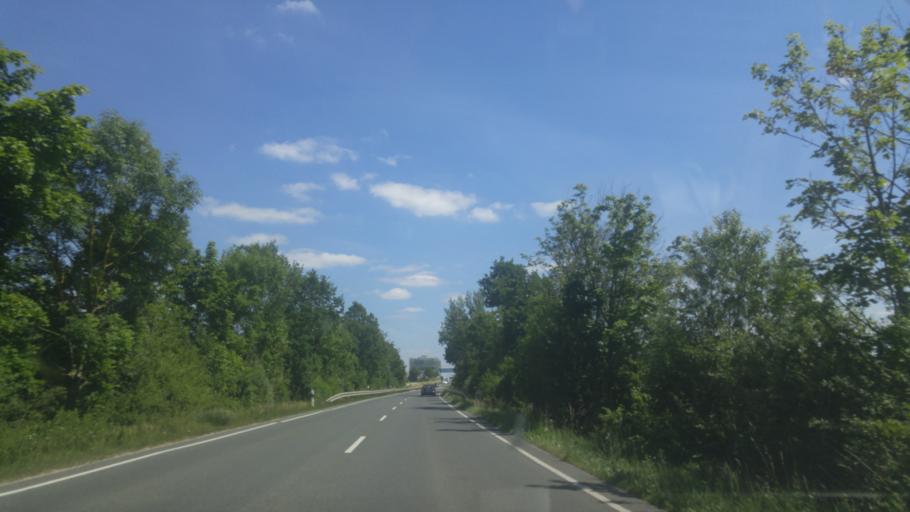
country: DE
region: Bavaria
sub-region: Regierungsbezirk Mittelfranken
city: Herzogenaurach
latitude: 49.5783
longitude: 10.8928
